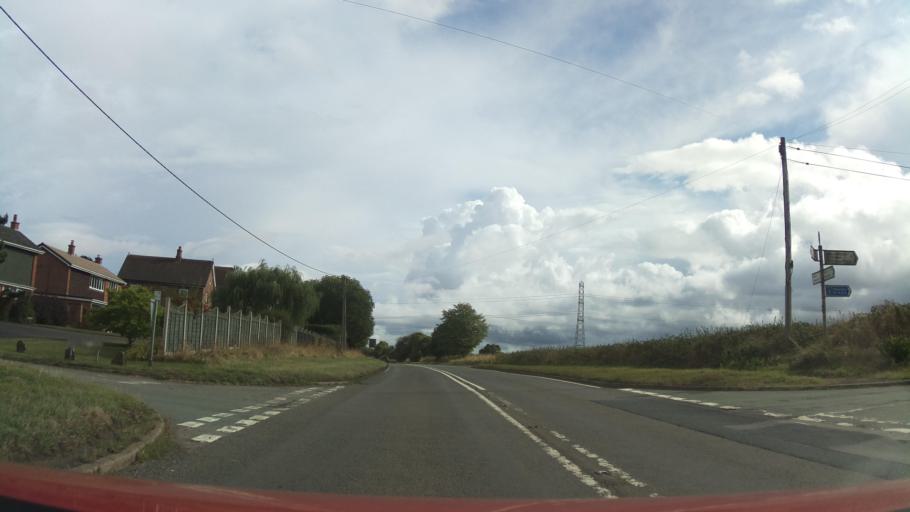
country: GB
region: England
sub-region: Telford and Wrekin
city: Madeley
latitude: 52.6103
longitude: -2.4106
